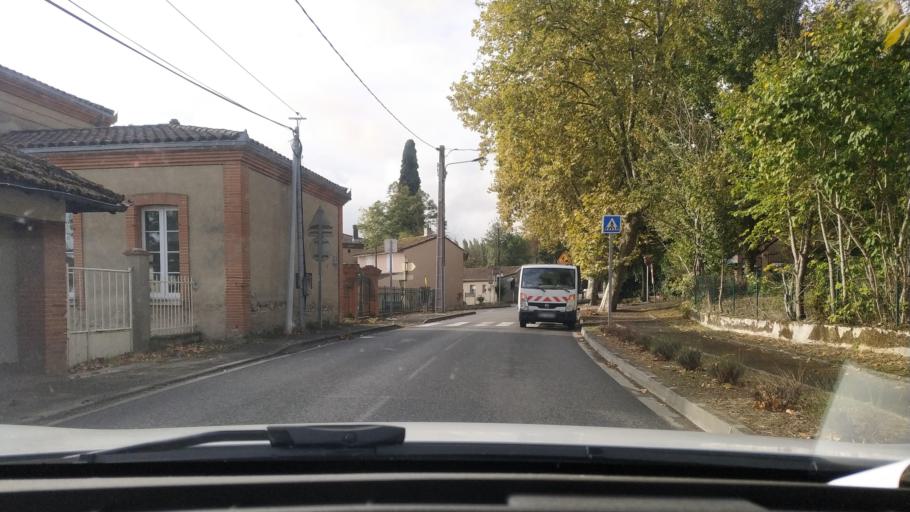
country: FR
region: Midi-Pyrenees
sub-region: Departement de la Haute-Garonne
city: Gaillac-Toulza
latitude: 43.2993
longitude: 1.4702
